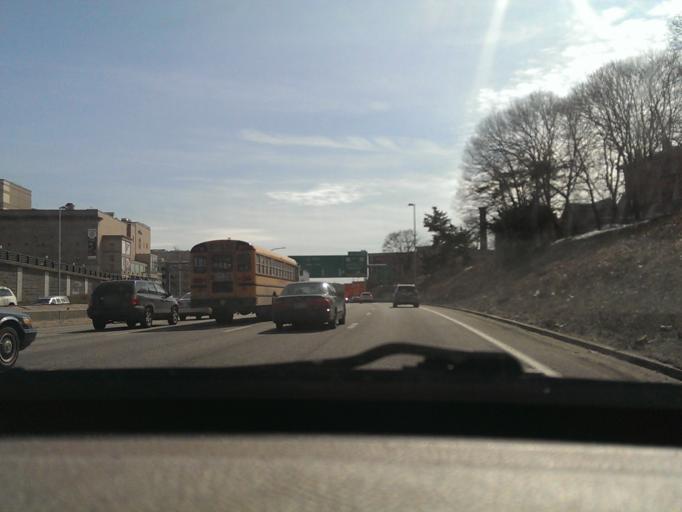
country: US
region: Rhode Island
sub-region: Providence County
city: Providence
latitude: 41.8319
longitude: -71.4177
